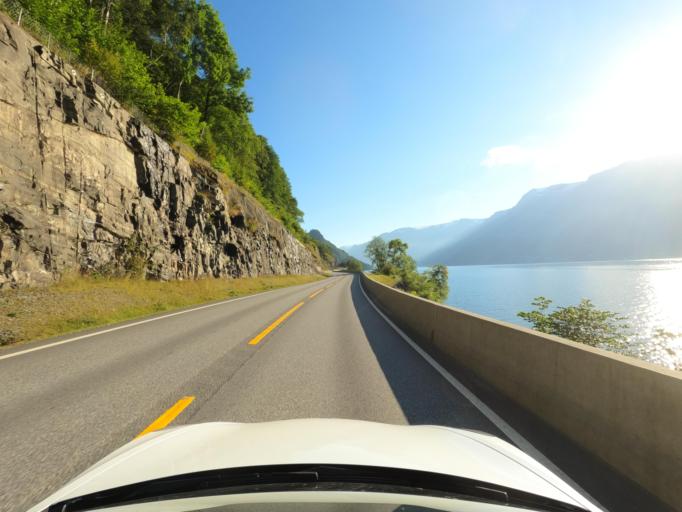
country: NO
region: Hordaland
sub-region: Ullensvang
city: Kinsarvik
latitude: 60.3062
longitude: 6.6453
